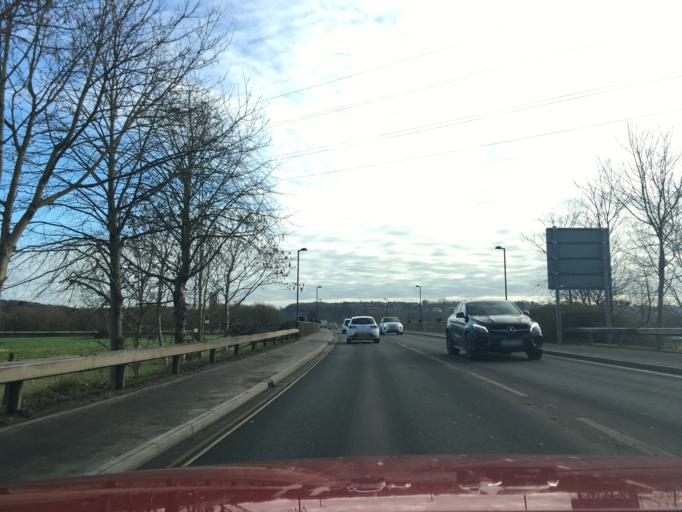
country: GB
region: England
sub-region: Staffordshire
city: Burton upon Trent
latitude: 52.7970
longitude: -1.6331
